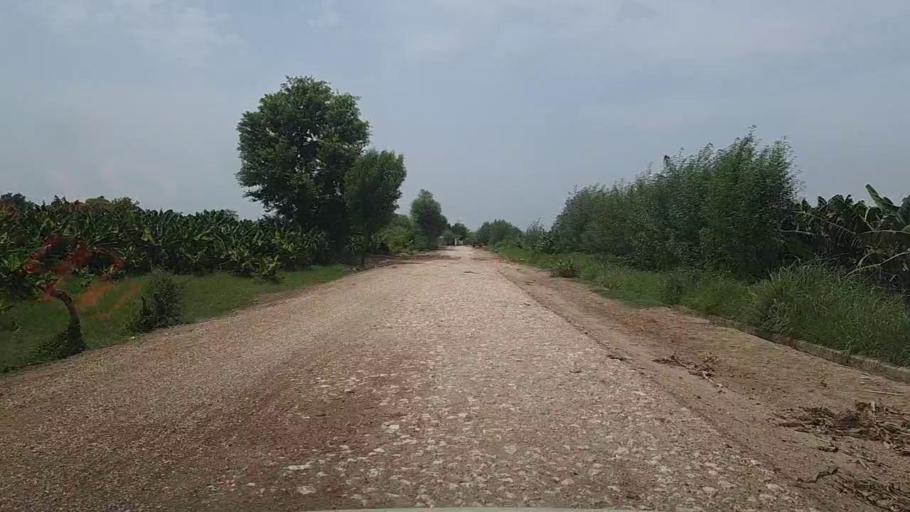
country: PK
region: Sindh
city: Karaundi
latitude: 26.9171
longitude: 68.3348
